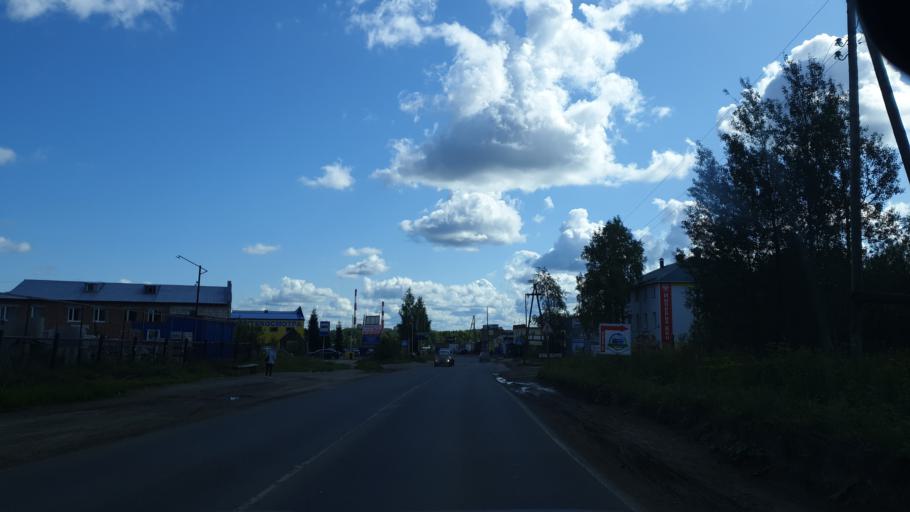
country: RU
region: Komi Republic
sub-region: Syktyvdinskiy Rayon
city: Syktyvkar
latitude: 61.6759
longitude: 50.7702
